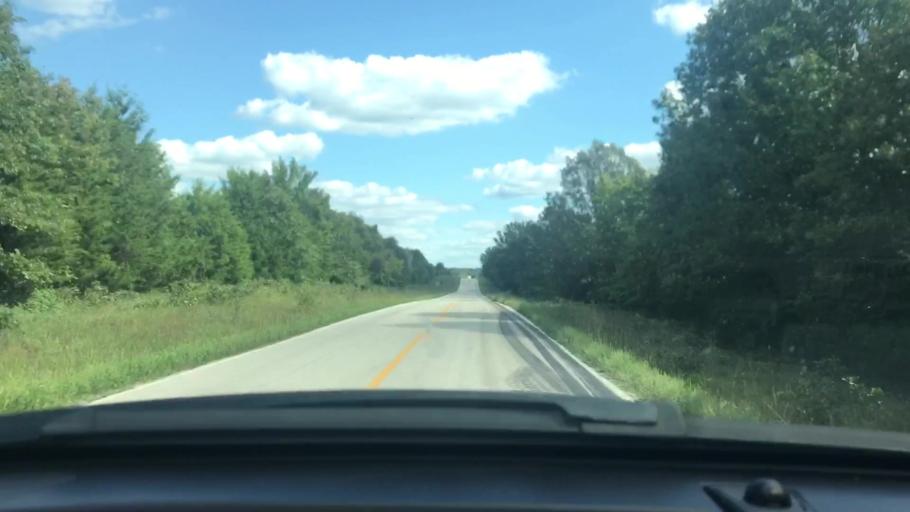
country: US
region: Missouri
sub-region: Wright County
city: Hartville
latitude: 37.3914
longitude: -92.4495
